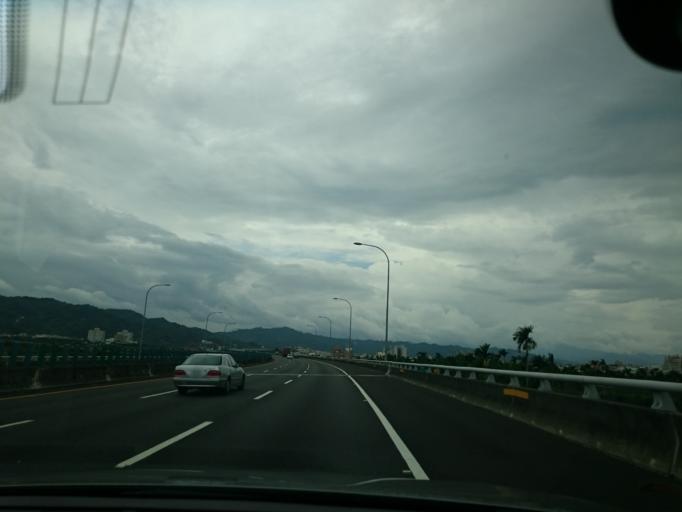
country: TW
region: Taiwan
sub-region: Nantou
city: Nantou
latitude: 23.9232
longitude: 120.6833
